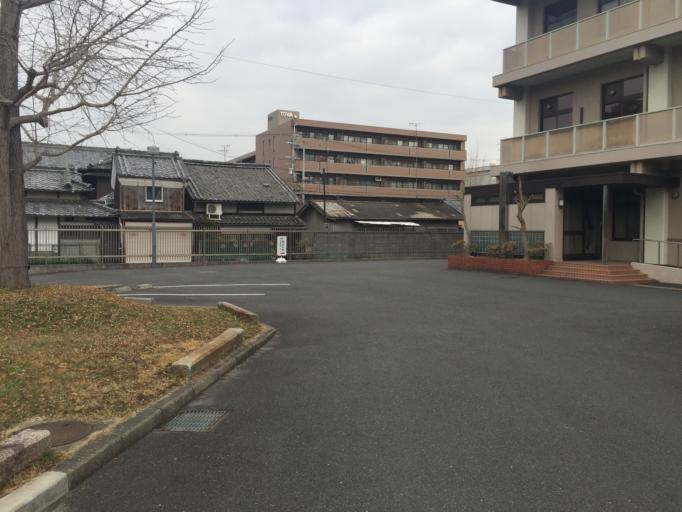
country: JP
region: Nara
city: Nara-shi
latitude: 34.6888
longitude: 135.8298
